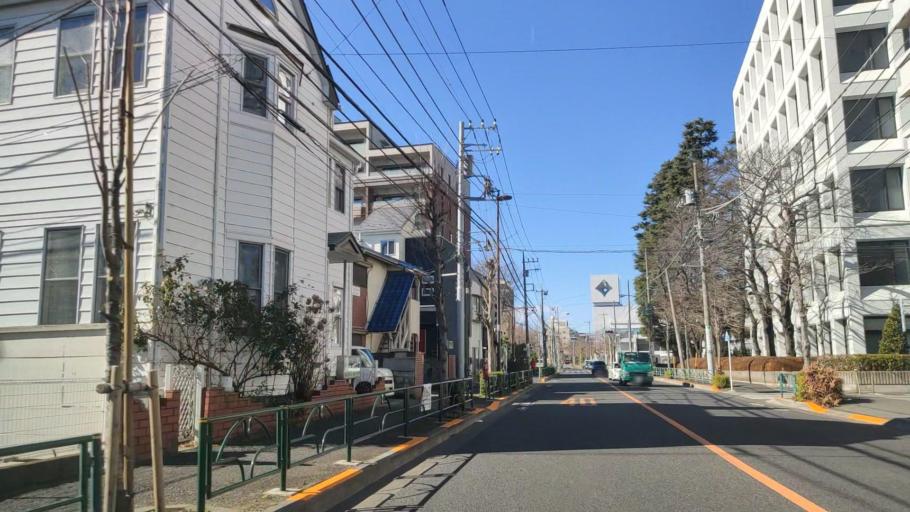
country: JP
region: Tokyo
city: Musashino
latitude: 35.7064
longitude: 139.5657
